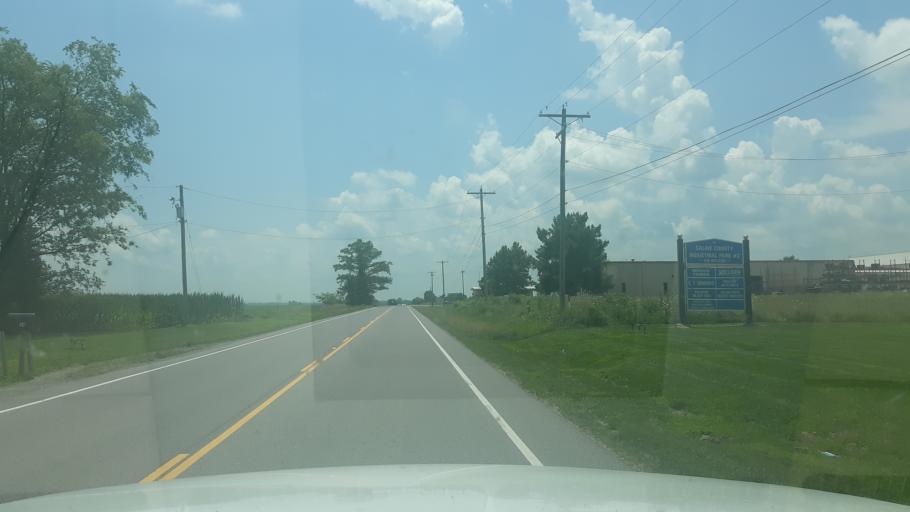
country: US
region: Illinois
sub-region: Saline County
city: Harrisburg
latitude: 37.8207
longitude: -88.5395
